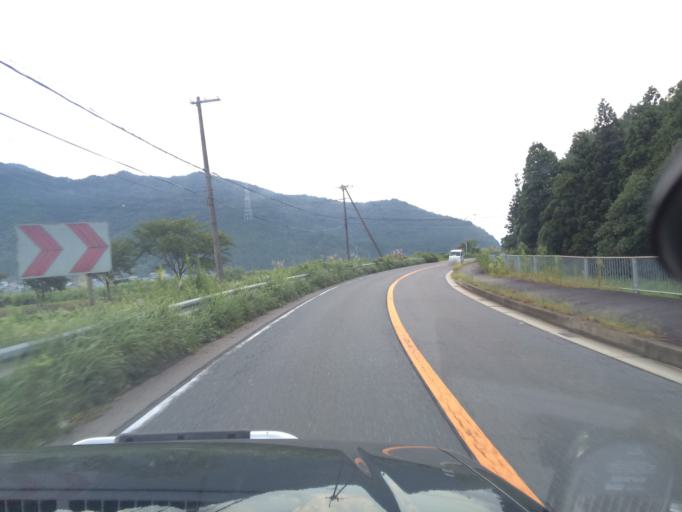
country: JP
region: Hyogo
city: Nishiwaki
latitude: 35.1106
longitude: 134.9950
